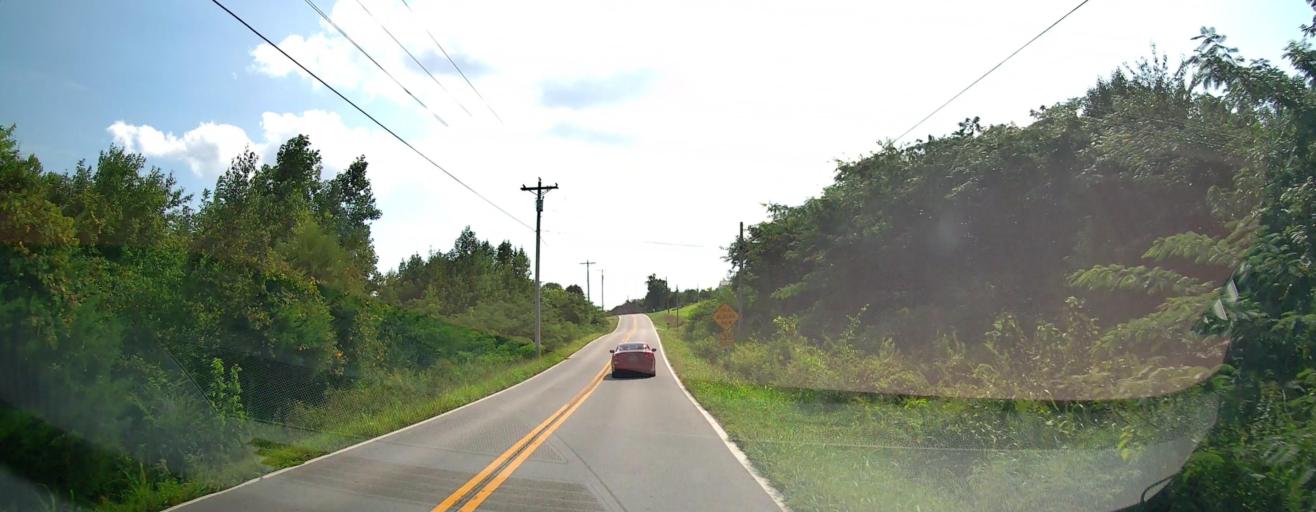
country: US
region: Georgia
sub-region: Catoosa County
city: Ringgold
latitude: 34.9459
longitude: -85.0807
